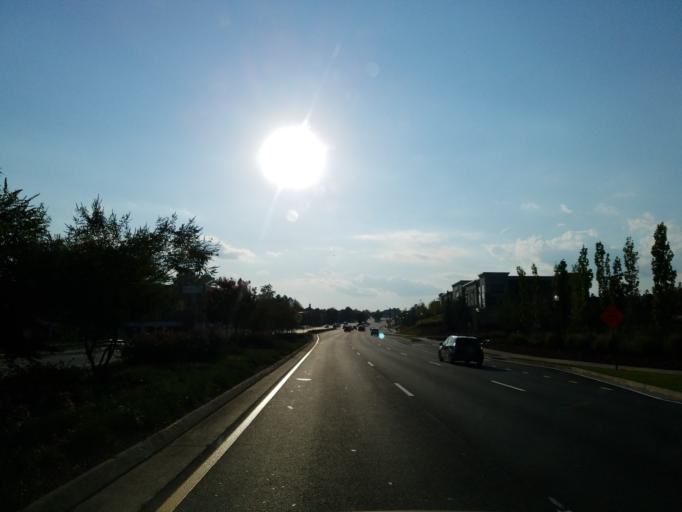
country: US
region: Georgia
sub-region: Fulton County
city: Alpharetta
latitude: 34.0687
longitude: -84.2740
